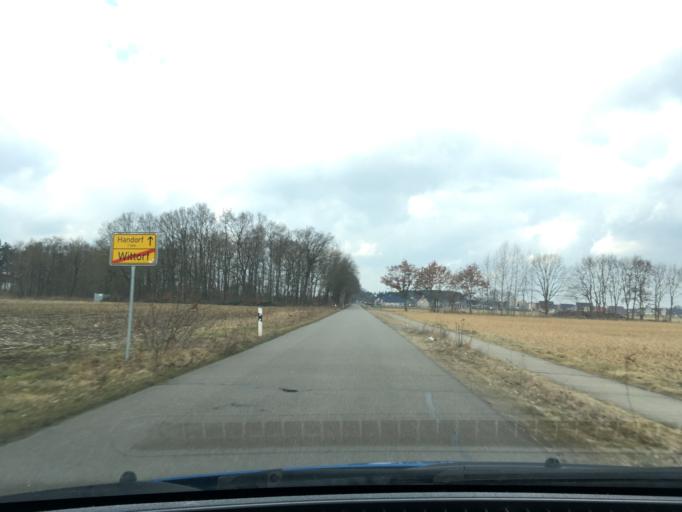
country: DE
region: Lower Saxony
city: Handorf
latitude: 53.3283
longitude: 10.3547
